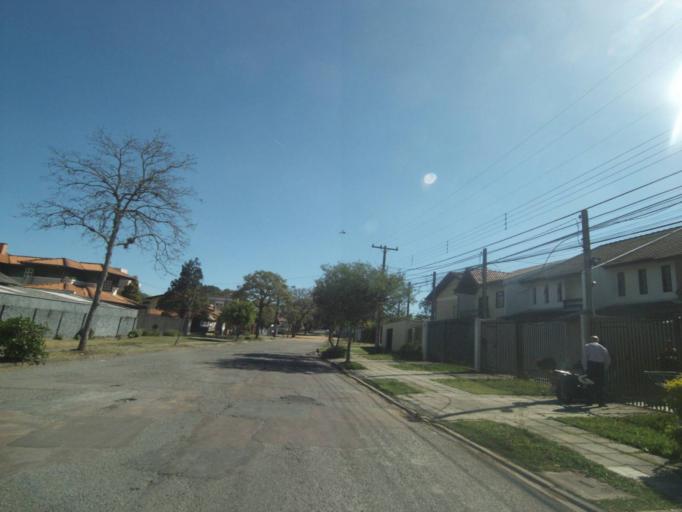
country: BR
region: Parana
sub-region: Curitiba
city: Curitiba
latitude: -25.3921
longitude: -49.2337
